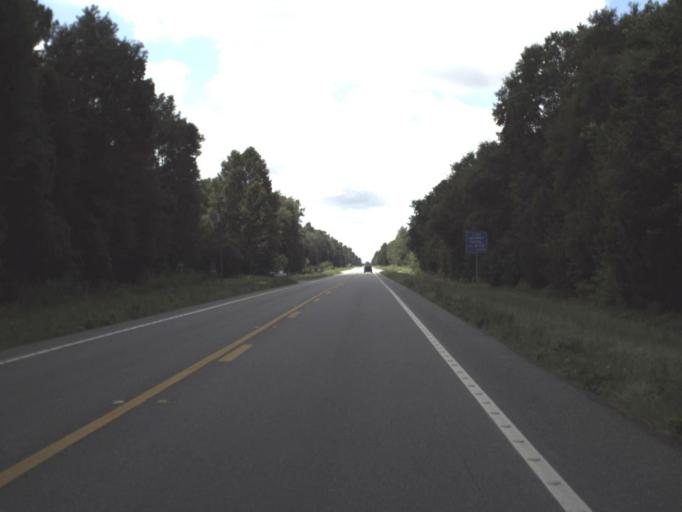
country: US
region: Florida
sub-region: Alachua County
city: High Springs
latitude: 29.8901
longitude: -82.8599
